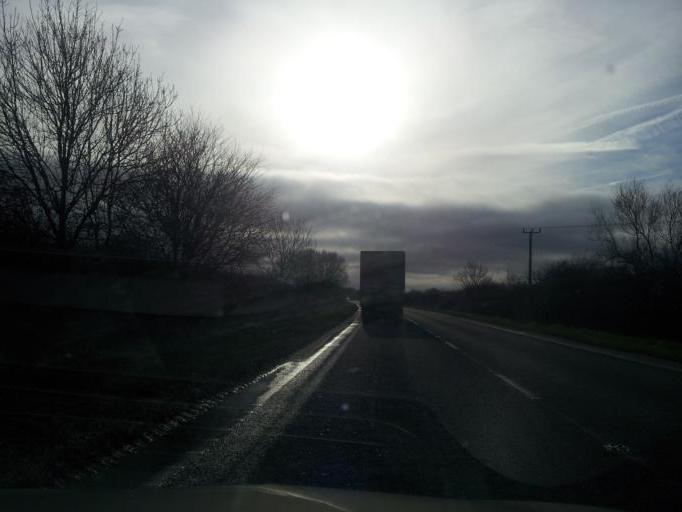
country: GB
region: England
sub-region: District of Rutland
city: Ketton
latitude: 52.6039
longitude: -0.5362
